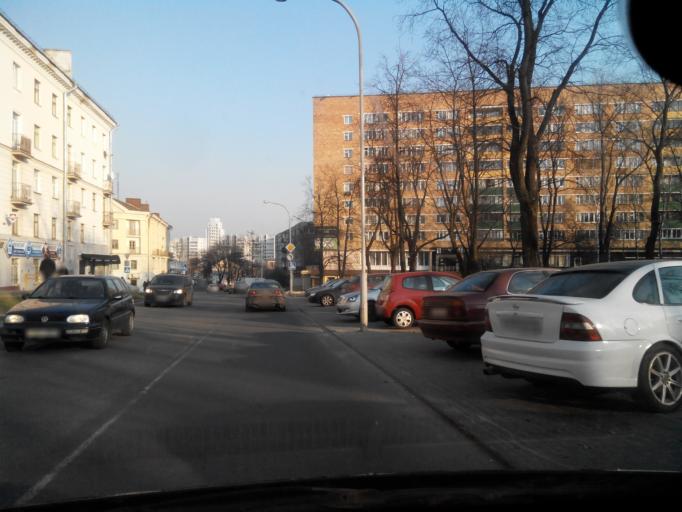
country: BY
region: Minsk
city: Minsk
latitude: 53.9056
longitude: 27.5431
